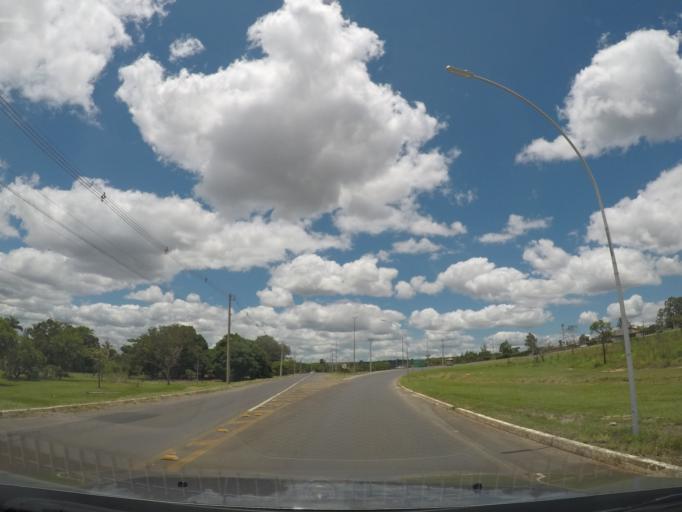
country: BR
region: Federal District
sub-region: Brasilia
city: Brasilia
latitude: -15.7599
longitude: -47.8119
